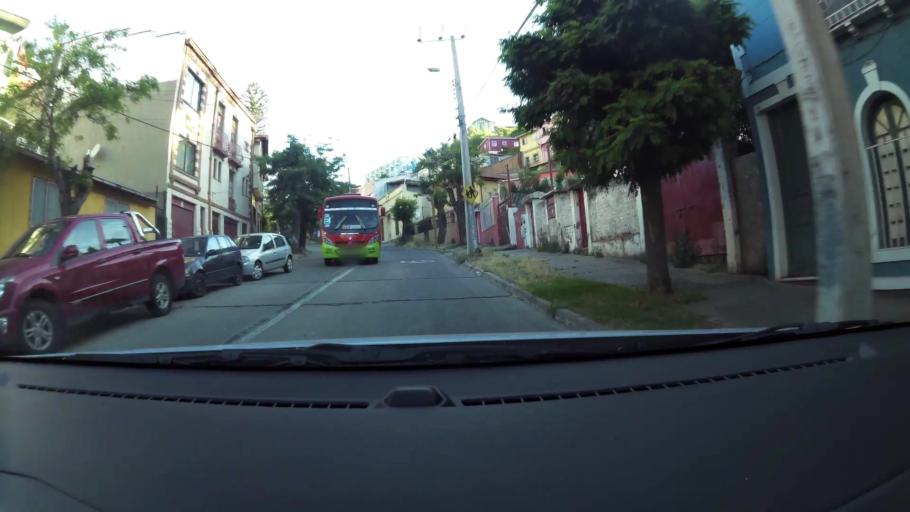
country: CL
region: Valparaiso
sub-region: Provincia de Valparaiso
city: Valparaiso
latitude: -33.0489
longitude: -71.6232
